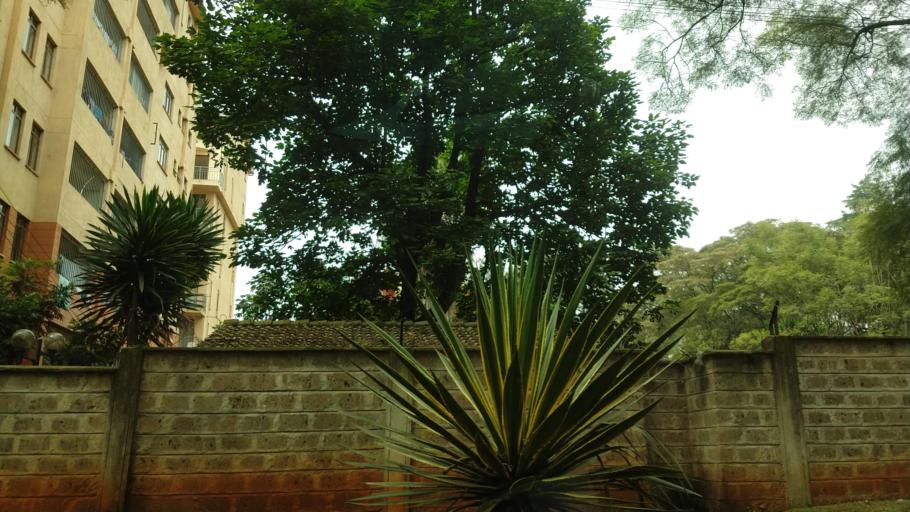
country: KE
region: Nairobi Area
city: Nairobi
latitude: -1.2967
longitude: 36.7768
